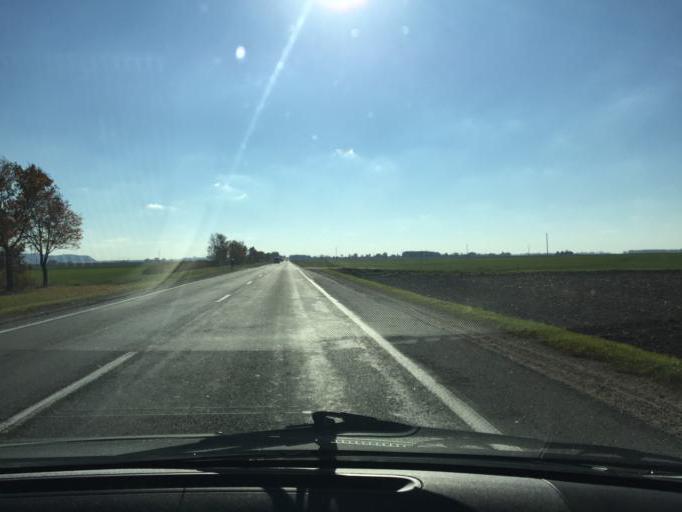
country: BY
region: Minsk
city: Slutsk
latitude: 52.9334
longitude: 27.4879
